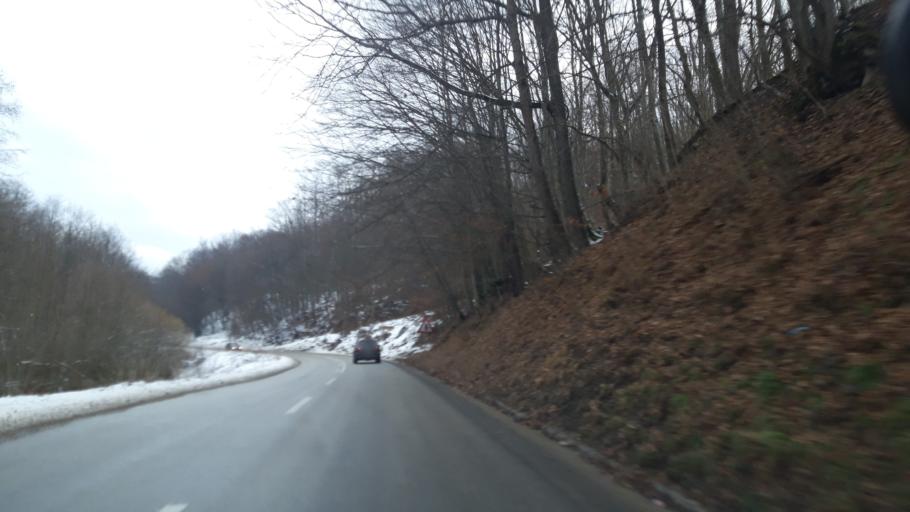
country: BA
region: Republika Srpska
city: Vlasenica
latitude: 44.1847
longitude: 19.0006
